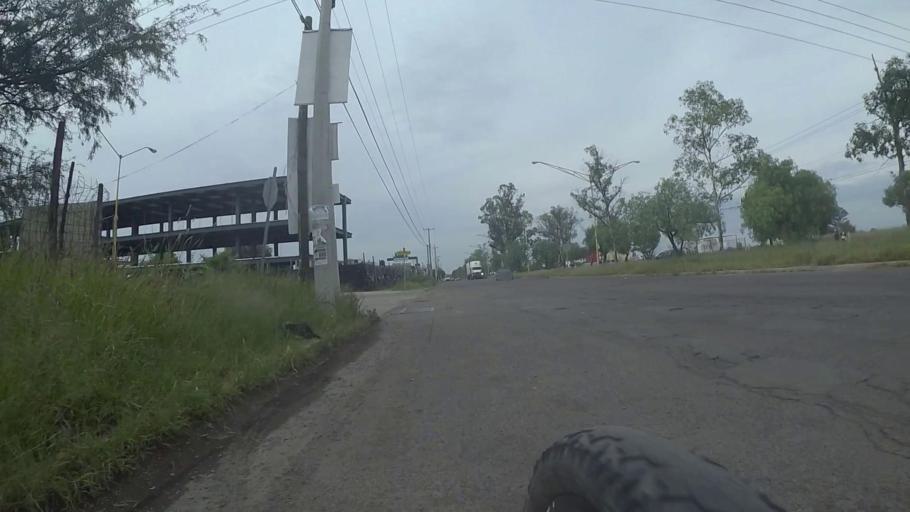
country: MX
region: Aguascalientes
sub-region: Aguascalientes
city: San Sebastian [Fraccionamiento]
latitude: 21.8363
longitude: -102.2938
